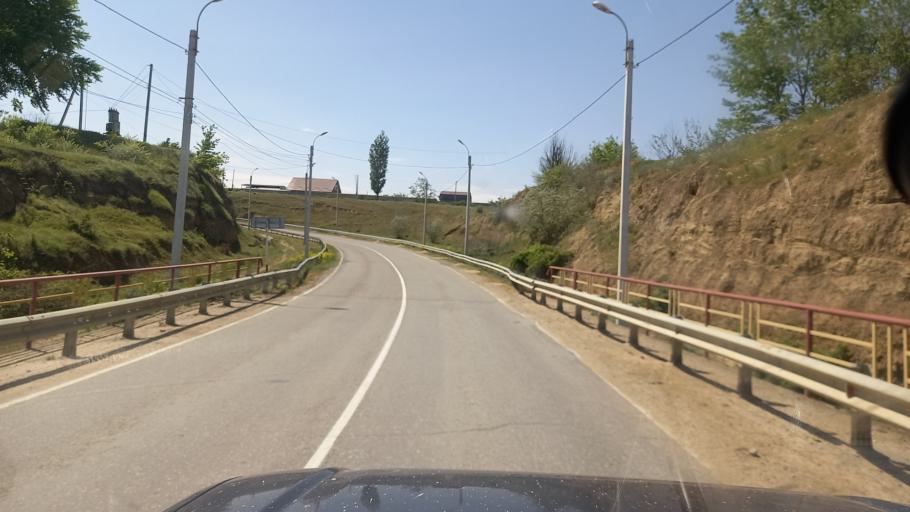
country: RU
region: Dagestan
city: Novaya Maka
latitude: 41.7379
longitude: 48.4444
